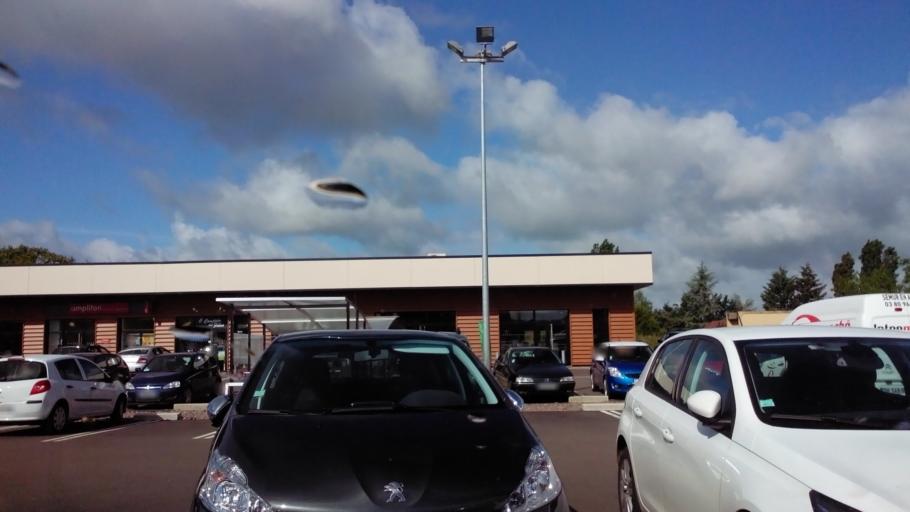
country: FR
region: Bourgogne
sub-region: Departement de la Cote-d'Or
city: Semur-en-Auxois
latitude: 47.4934
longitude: 4.3414
